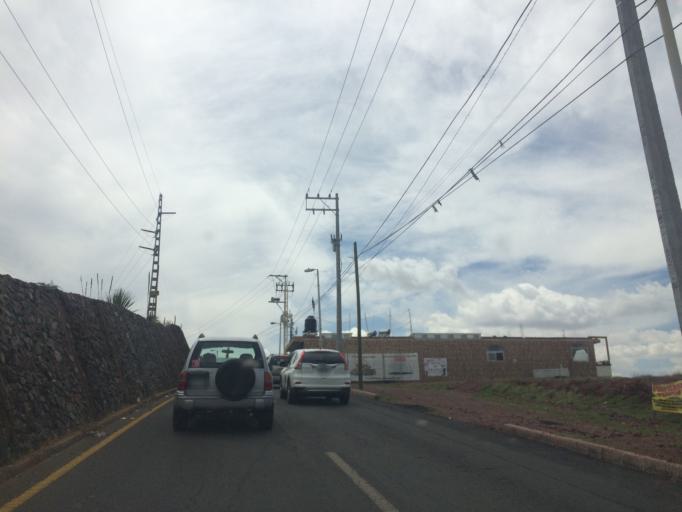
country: MX
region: Zacatecas
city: Zacatecas
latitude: 22.7607
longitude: -102.5711
